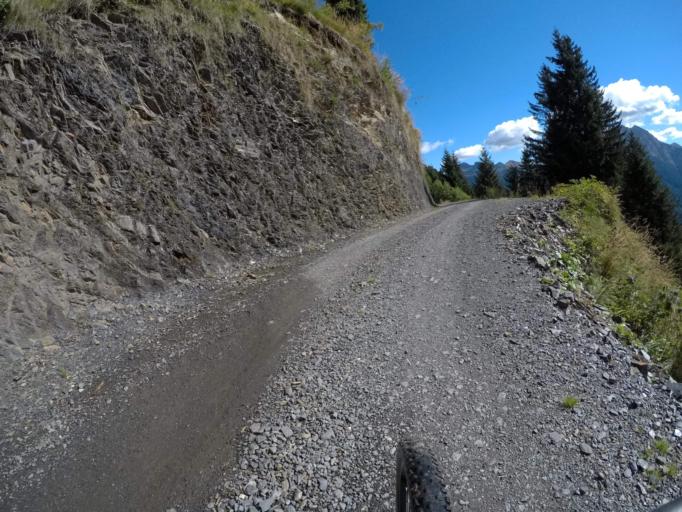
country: IT
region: Friuli Venezia Giulia
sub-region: Provincia di Udine
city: Ligosullo
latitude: 46.5663
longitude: 13.0858
